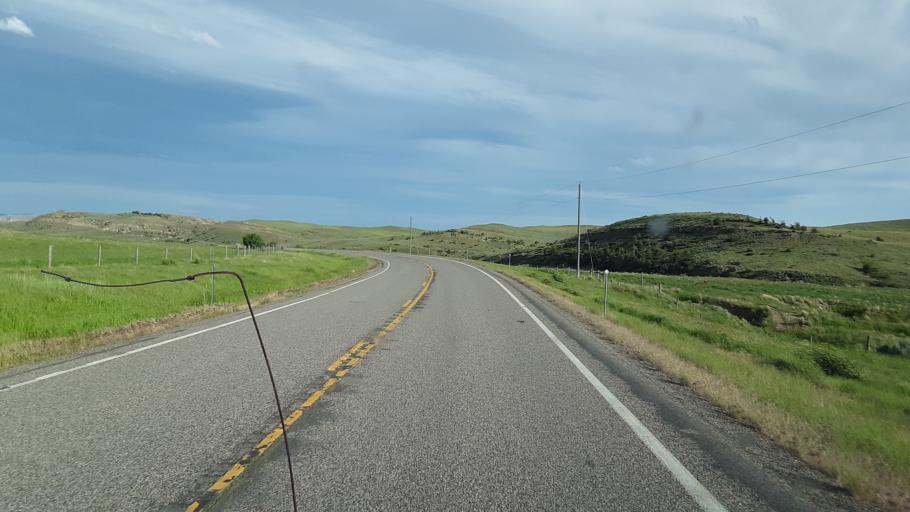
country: US
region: Montana
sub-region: Carbon County
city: Red Lodge
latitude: 45.1630
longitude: -109.0965
